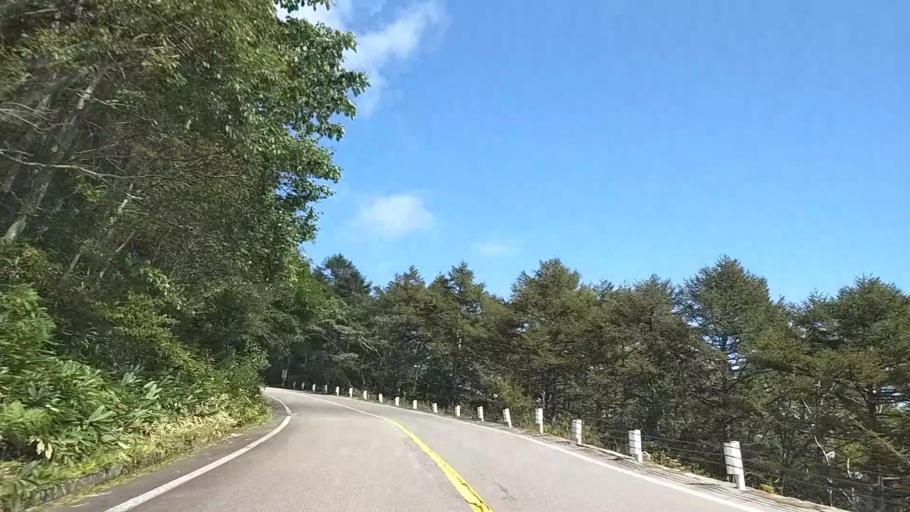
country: JP
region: Nagano
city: Suwa
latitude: 36.1511
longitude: 138.1416
